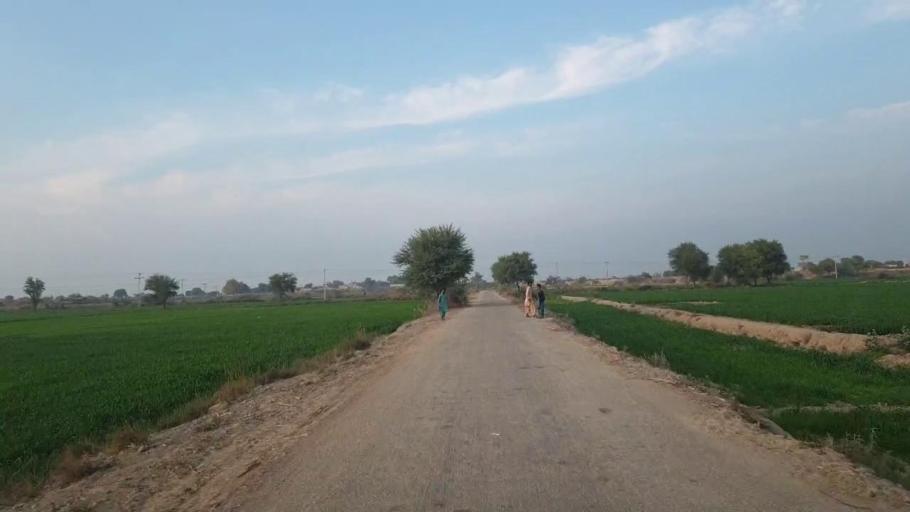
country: PK
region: Sindh
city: Shahpur Chakar
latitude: 26.1169
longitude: 68.5465
